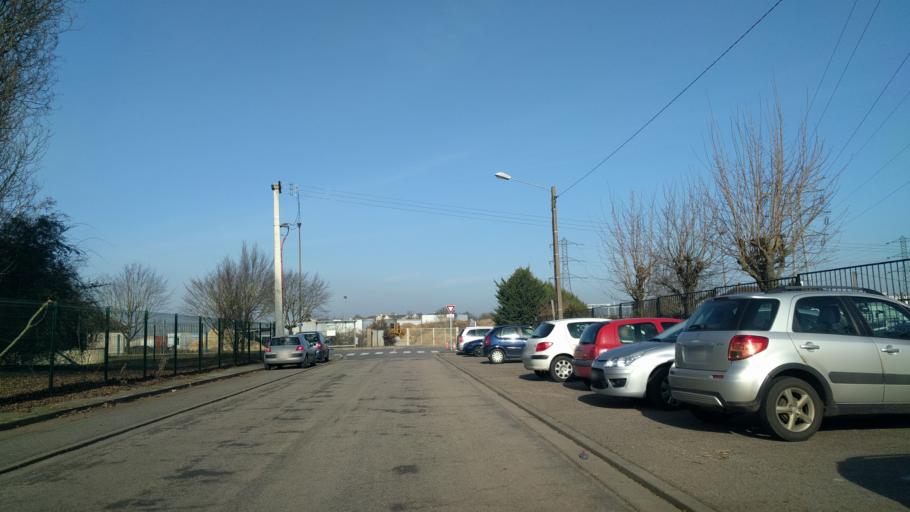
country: FR
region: Haute-Normandie
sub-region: Departement de l'Eure
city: Evreux
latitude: 49.0189
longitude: 1.1800
